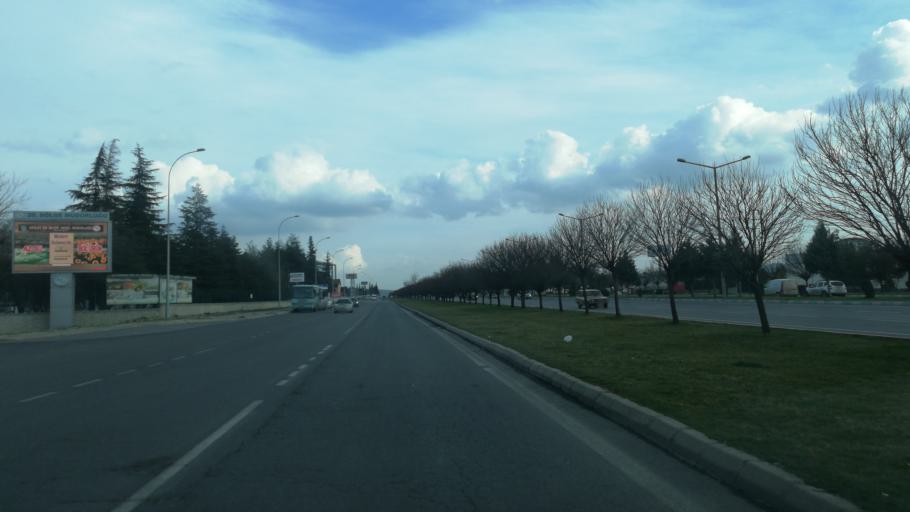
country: TR
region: Kahramanmaras
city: Kahramanmaras
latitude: 37.5382
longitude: 36.9784
